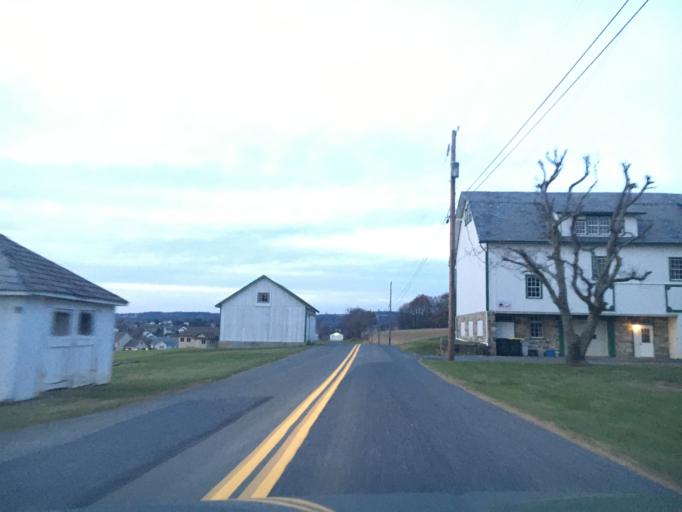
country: US
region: Pennsylvania
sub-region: Lehigh County
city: Schnecksville
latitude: 40.6934
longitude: -75.5784
